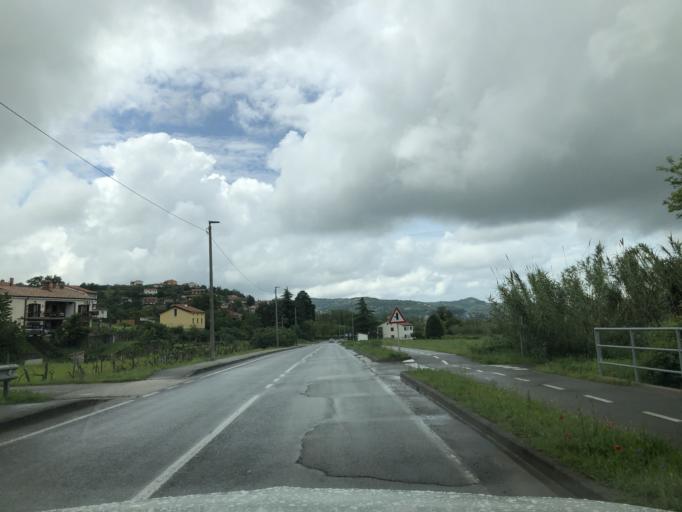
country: SI
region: Koper-Capodistria
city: Prade
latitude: 45.5165
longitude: 13.7667
